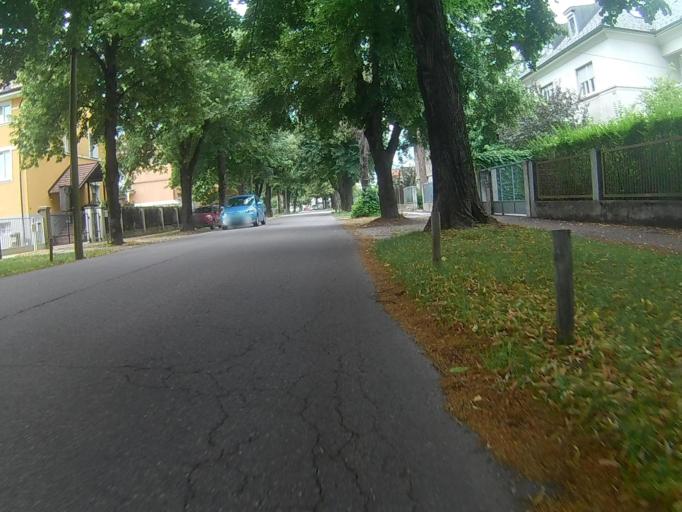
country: SI
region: Maribor
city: Maribor
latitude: 46.5651
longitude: 15.6329
